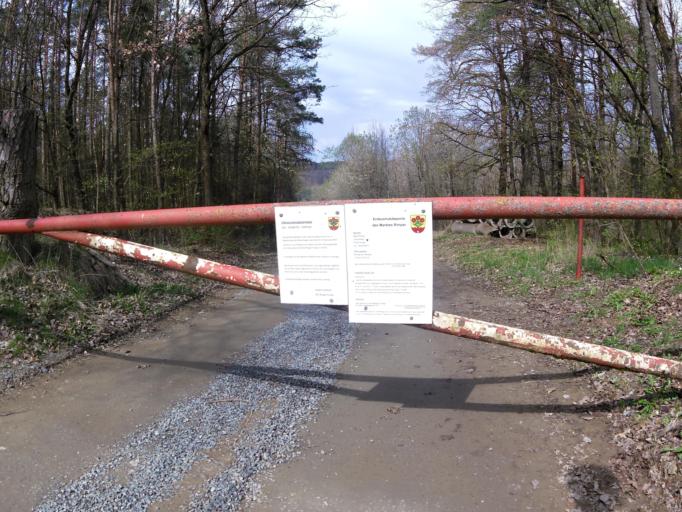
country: DE
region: Bavaria
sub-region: Regierungsbezirk Unterfranken
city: Rimpar
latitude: 49.8682
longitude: 9.9436
